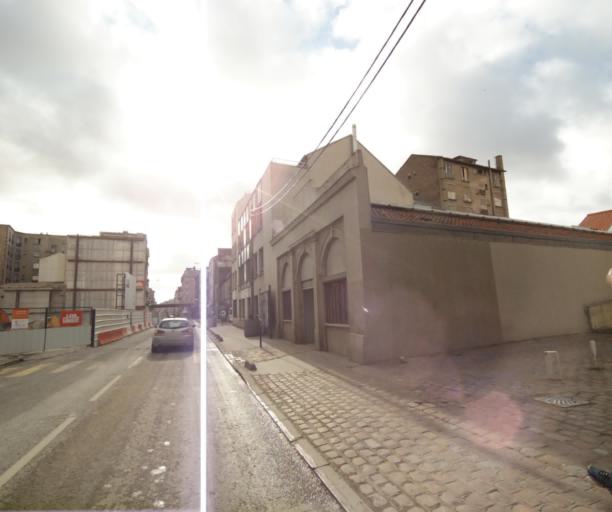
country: FR
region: Ile-de-France
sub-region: Paris
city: Saint-Ouen
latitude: 48.9095
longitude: 2.3386
